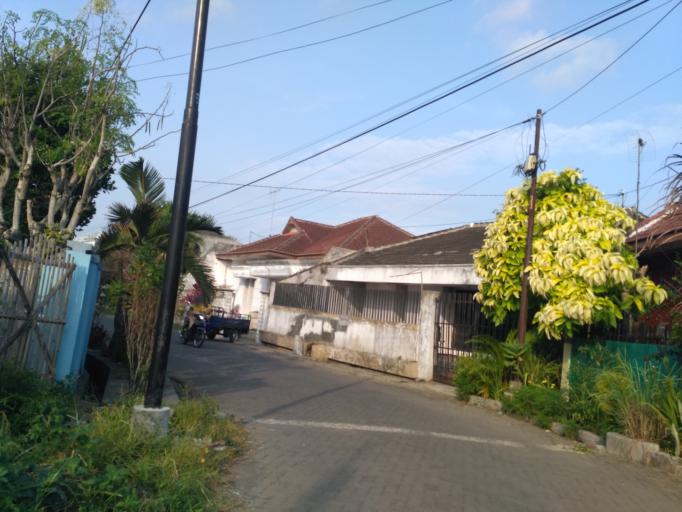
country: ID
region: East Java
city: Malang
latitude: -7.9375
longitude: 112.6357
